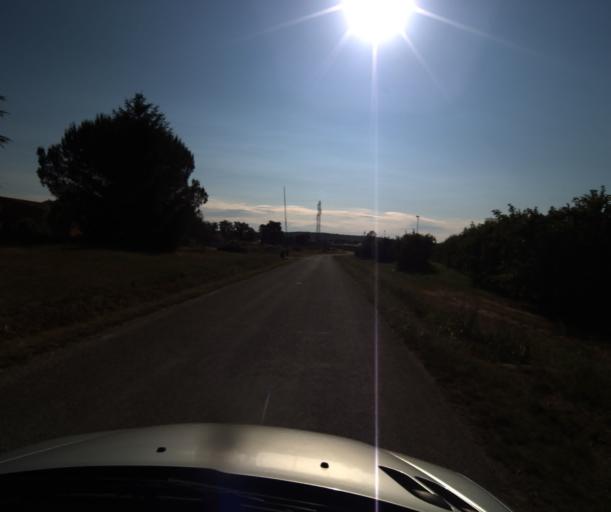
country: FR
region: Midi-Pyrenees
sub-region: Departement du Tarn-et-Garonne
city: Bressols
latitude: 43.9684
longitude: 1.3215
